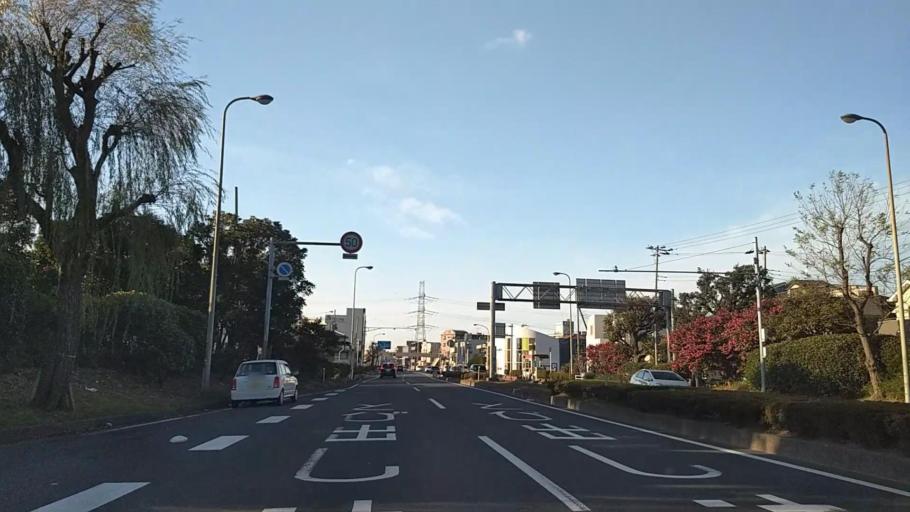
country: JP
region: Tokyo
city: Urayasu
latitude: 35.6571
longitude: 139.9064
